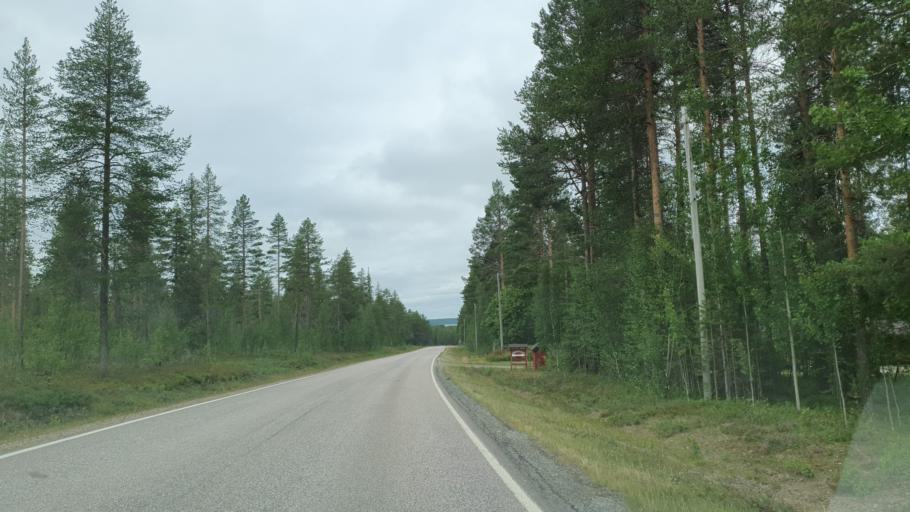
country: FI
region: Lapland
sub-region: Pohjois-Lappi
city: Sodankylae
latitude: 67.4164
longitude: 26.2658
